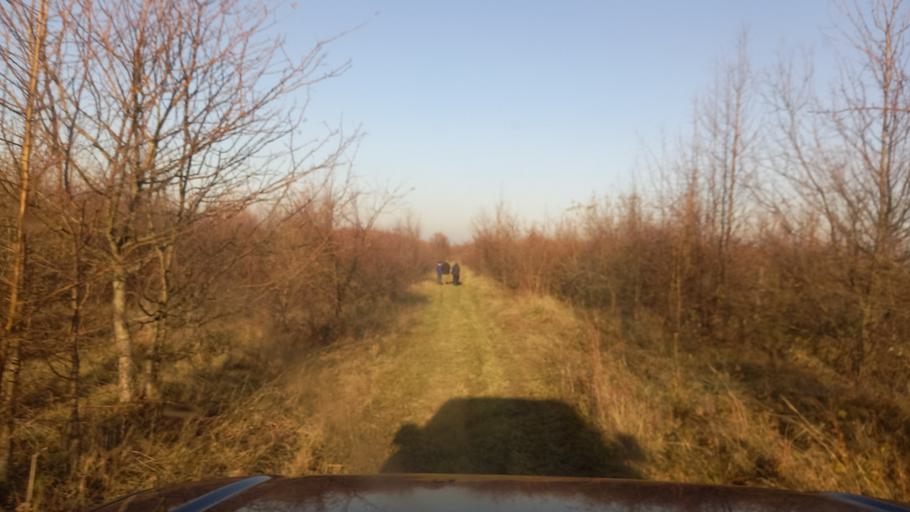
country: RU
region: Krasnodarskiy
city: Azovskaya
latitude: 44.8086
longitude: 38.5938
